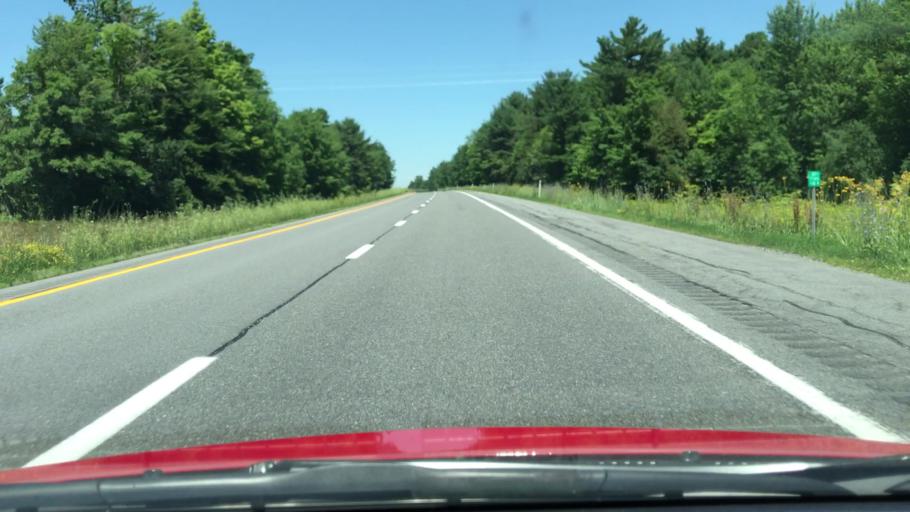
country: US
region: New York
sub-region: Clinton County
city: Champlain
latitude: 44.9246
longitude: -73.4457
